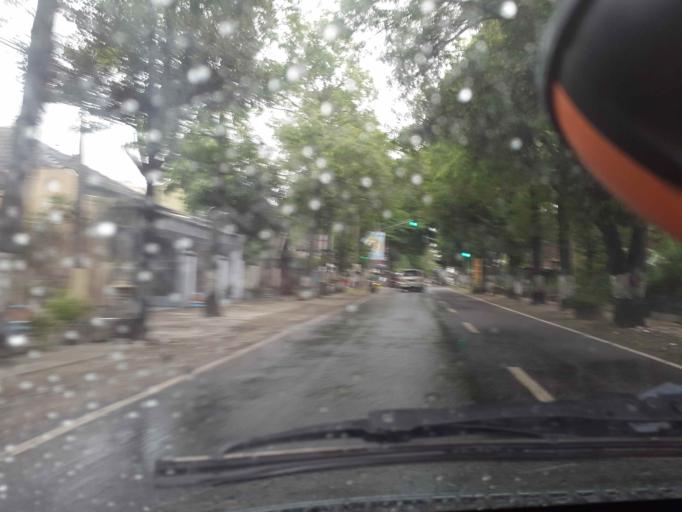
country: ID
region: Central Java
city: Sragen
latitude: -7.4353
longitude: 111.0222
